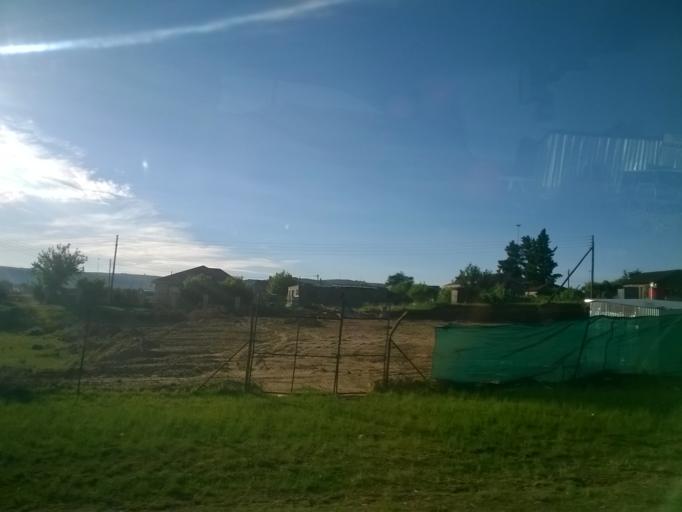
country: LS
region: Maseru
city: Maseru
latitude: -29.2715
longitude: 27.5338
